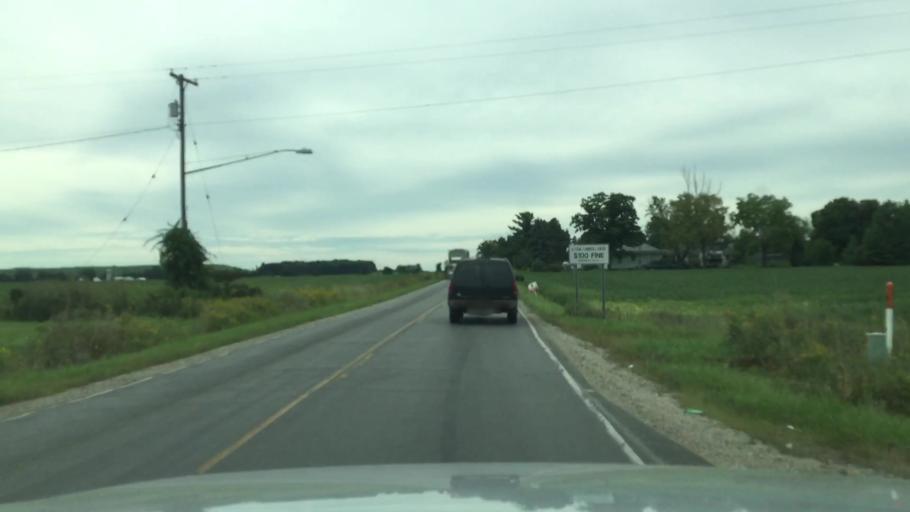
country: US
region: Michigan
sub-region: Shiawassee County
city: Durand
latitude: 42.9993
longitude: -83.9868
